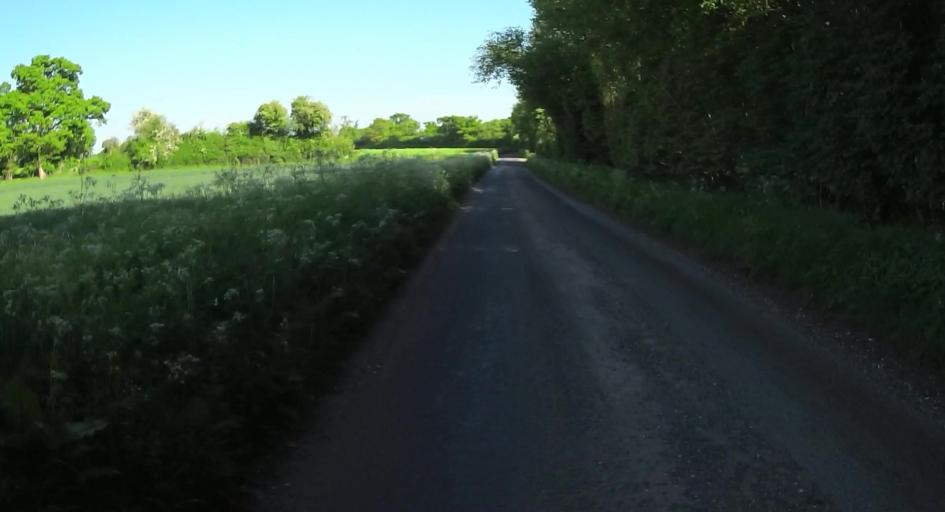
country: GB
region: England
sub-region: Hampshire
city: Overton
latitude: 51.1655
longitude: -1.1875
